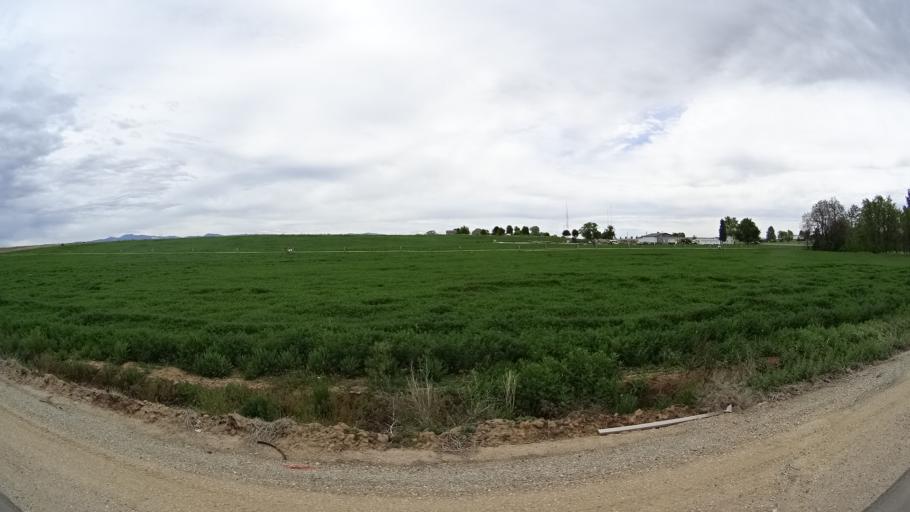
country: US
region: Idaho
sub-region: Ada County
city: Meridian
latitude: 43.5628
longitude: -116.4138
